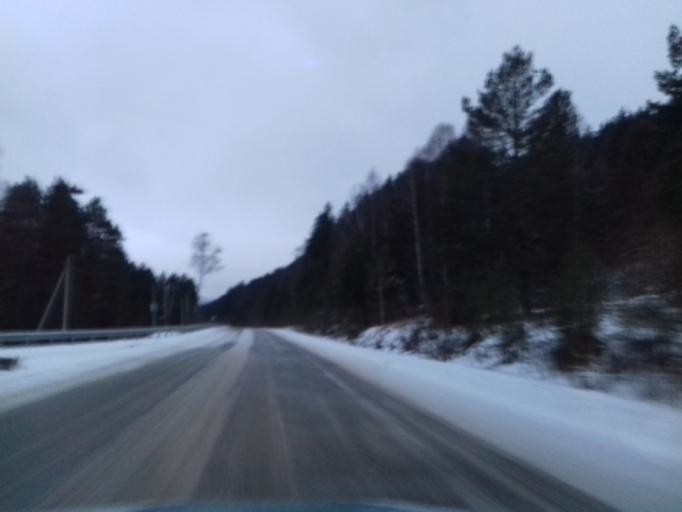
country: RU
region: Bashkortostan
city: Lomovka
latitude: 53.8618
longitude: 58.0118
